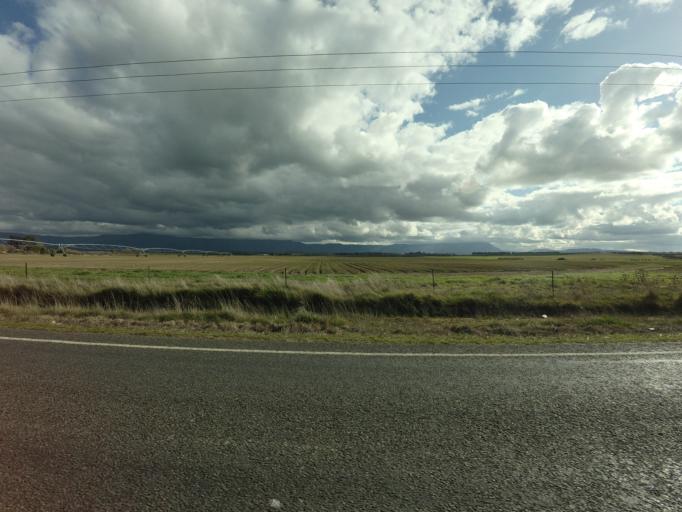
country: AU
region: Tasmania
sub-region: Northern Midlands
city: Longford
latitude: -41.7087
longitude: 147.0803
